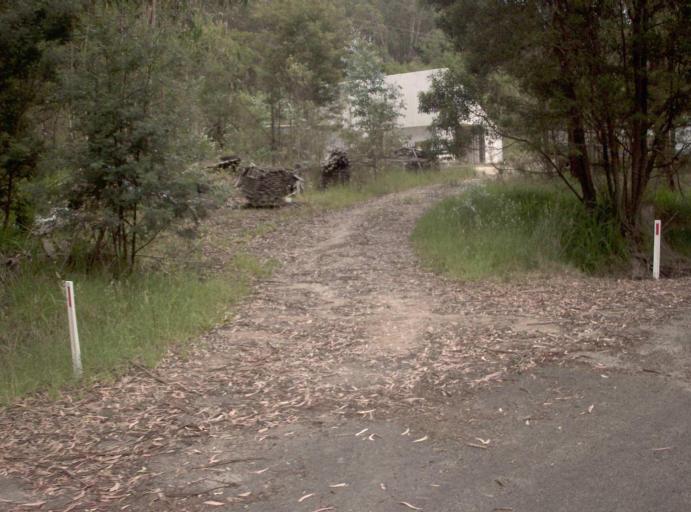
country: AU
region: New South Wales
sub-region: Bombala
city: Bombala
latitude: -37.4308
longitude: 149.1979
